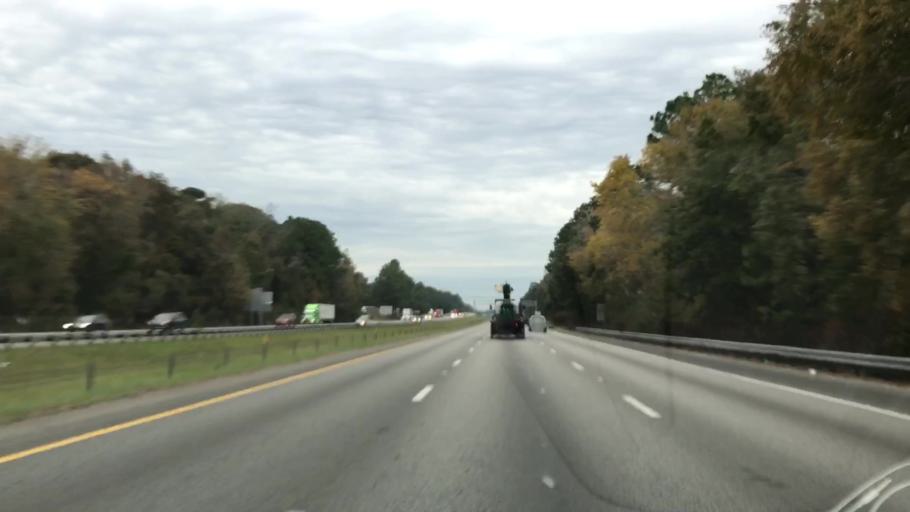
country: US
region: South Carolina
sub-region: Berkeley County
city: Ladson
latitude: 32.9868
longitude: -80.0812
